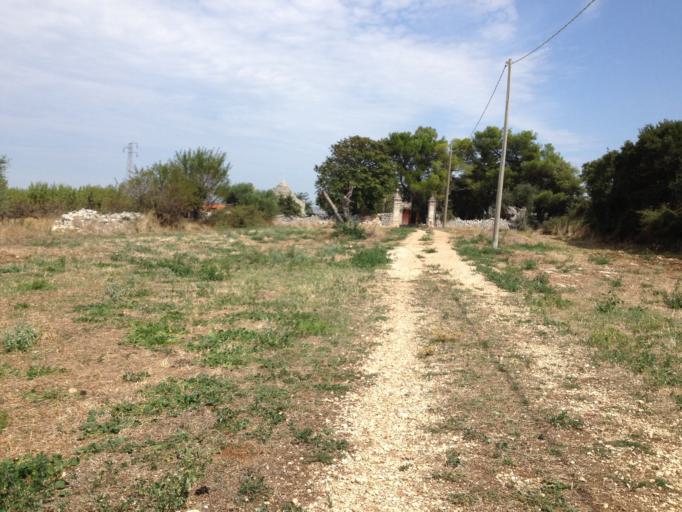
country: IT
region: Apulia
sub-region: Provincia di Bari
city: Gioia del Colle
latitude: 40.8292
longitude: 16.9900
